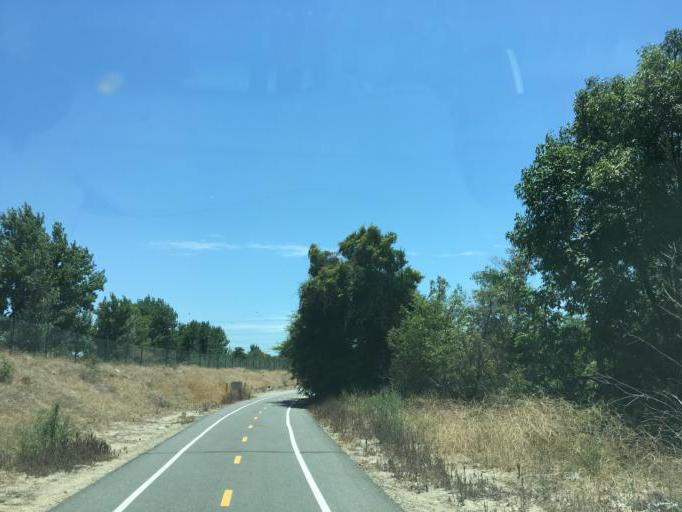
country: US
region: California
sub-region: Los Angeles County
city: South San Gabriel
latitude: 34.0406
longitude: -118.0739
